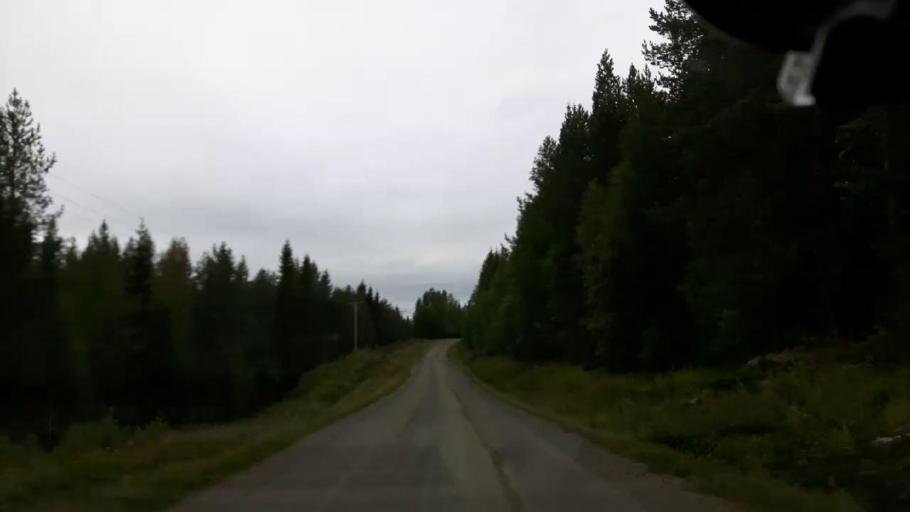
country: SE
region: Vaesternorrland
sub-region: Ange Kommun
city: Fransta
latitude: 62.8604
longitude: 15.9832
